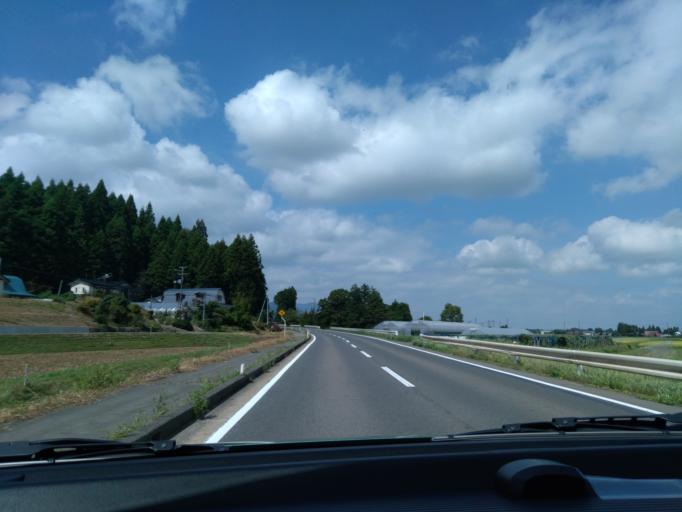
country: JP
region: Iwate
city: Hanamaki
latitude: 39.5361
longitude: 141.1113
